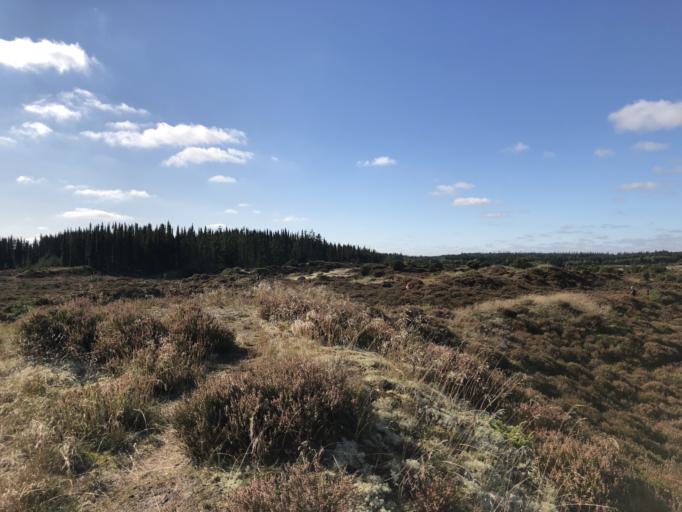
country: DK
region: Central Jutland
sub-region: Holstebro Kommune
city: Holstebro
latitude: 56.2501
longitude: 8.4904
